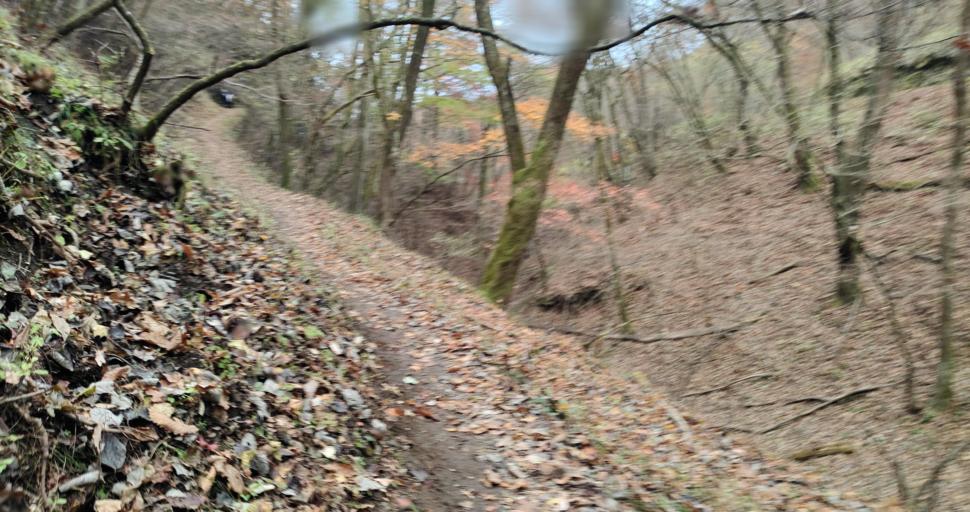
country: JP
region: Nagano
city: Saku
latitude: 36.2221
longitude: 138.6159
